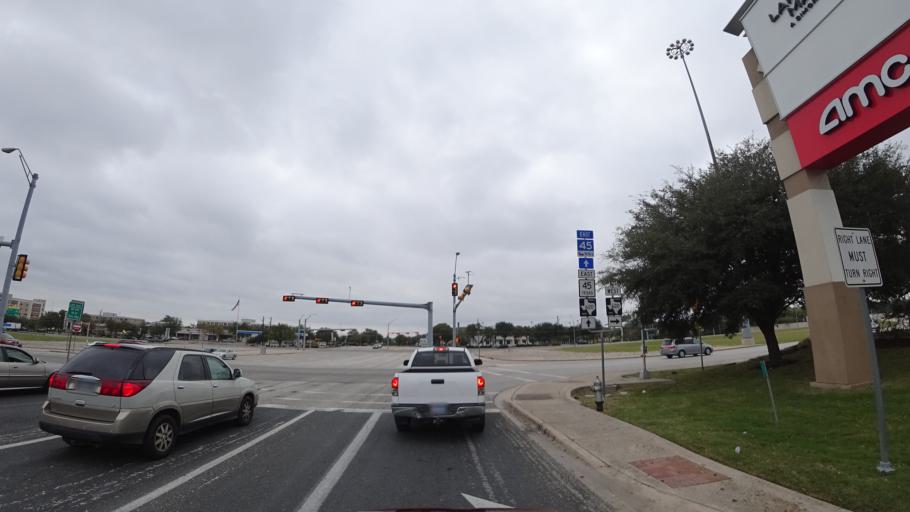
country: US
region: Texas
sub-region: Williamson County
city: Anderson Mill
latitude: 30.4670
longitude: -97.8046
